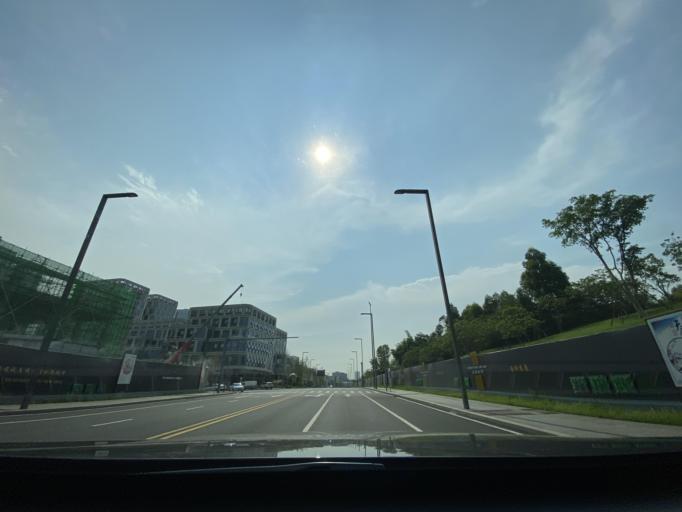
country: CN
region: Sichuan
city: Dongsheng
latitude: 30.3925
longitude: 104.0881
